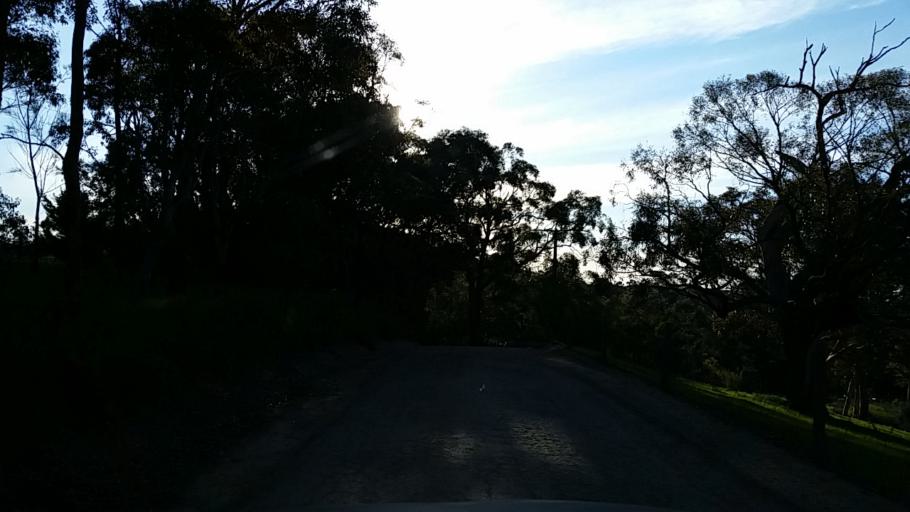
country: AU
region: South Australia
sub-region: Mount Barker
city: Meadows
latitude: -35.2297
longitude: 138.7423
